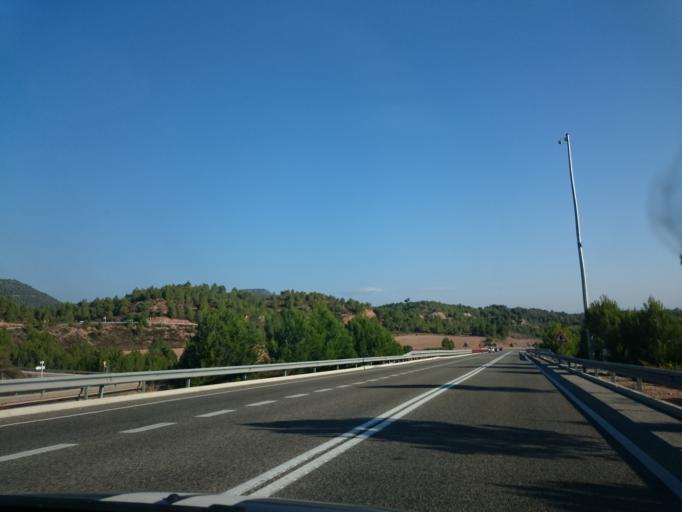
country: ES
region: Catalonia
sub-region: Provincia de Barcelona
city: Castellfollit del Boix
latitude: 41.6574
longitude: 1.7211
